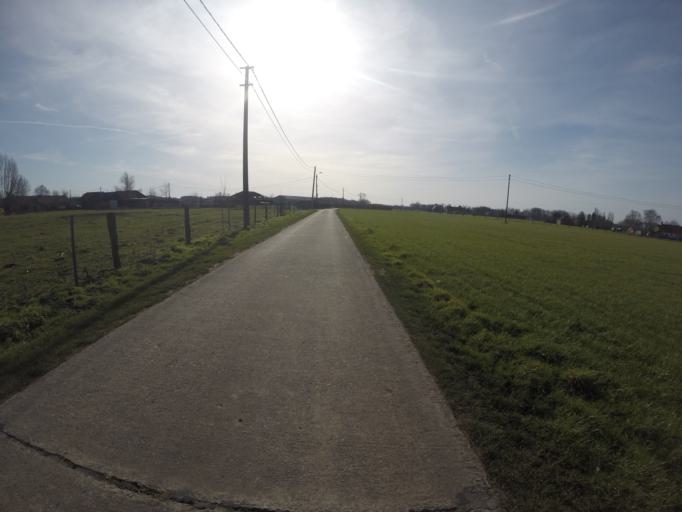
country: BE
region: Flanders
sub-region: Provincie West-Vlaanderen
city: Oostkamp
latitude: 51.1161
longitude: 3.2639
